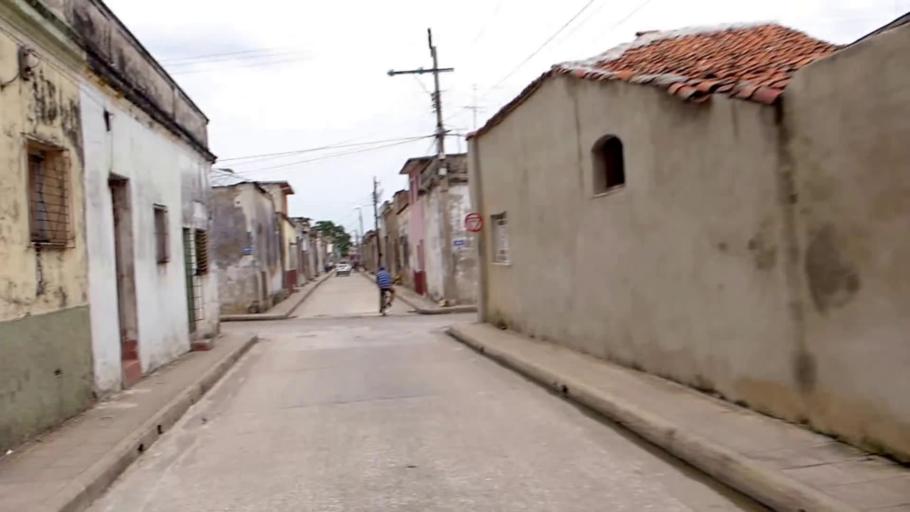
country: CU
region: Camaguey
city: Camaguey
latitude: 21.3808
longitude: -77.9232
